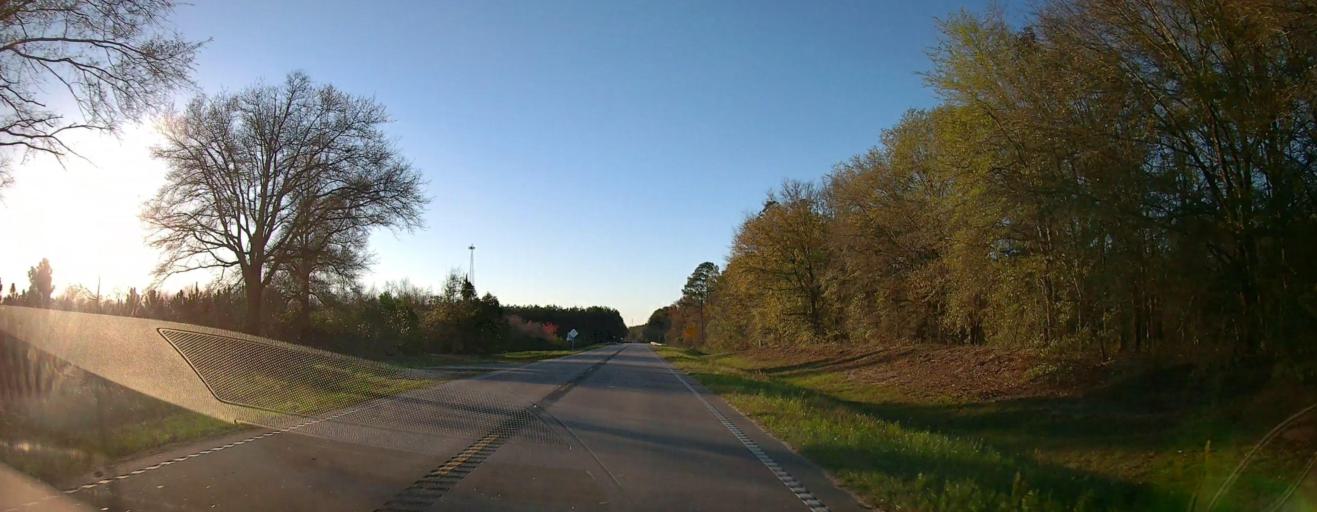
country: US
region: Georgia
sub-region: Wilcox County
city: Rochelle
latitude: 31.9546
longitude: -83.5780
